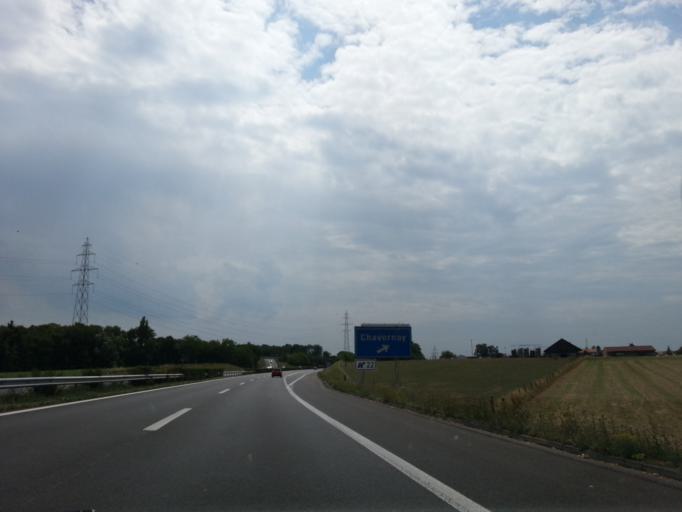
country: CH
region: Vaud
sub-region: Jura-Nord vaudois District
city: Chavornay
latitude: 46.7111
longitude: 6.5792
